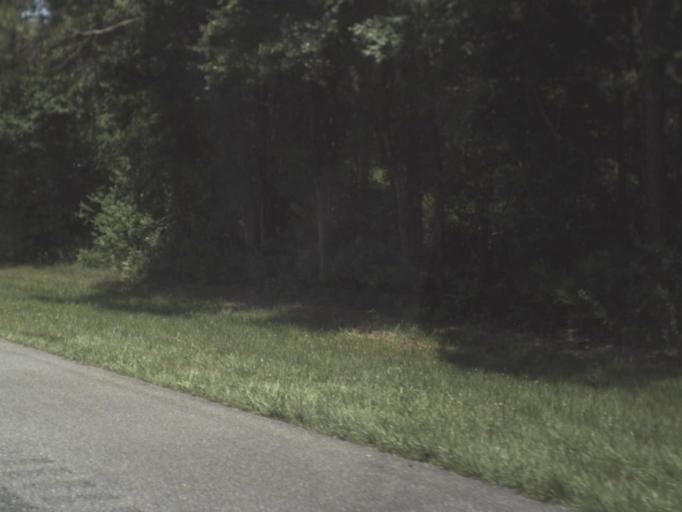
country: US
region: Florida
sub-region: Columbia County
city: Watertown
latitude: 30.2502
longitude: -82.5327
